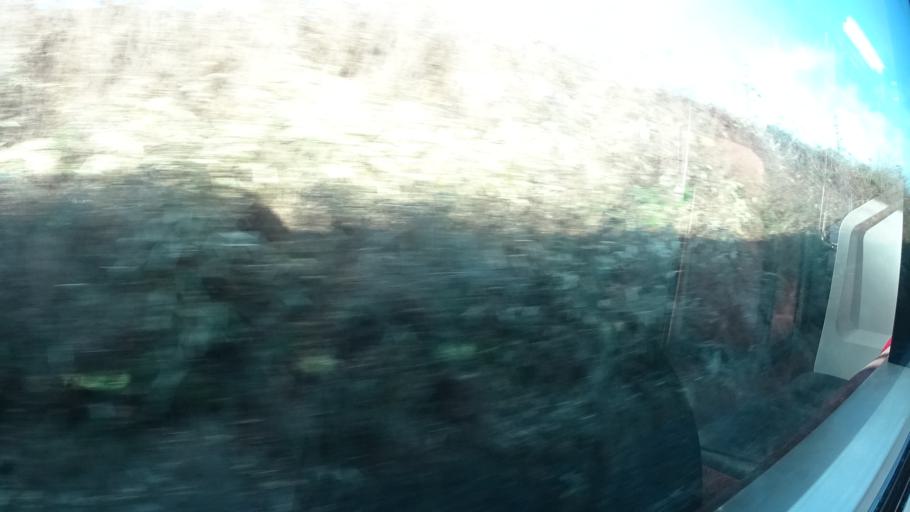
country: JP
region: Fukushima
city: Namie
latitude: 37.3536
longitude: 140.9930
